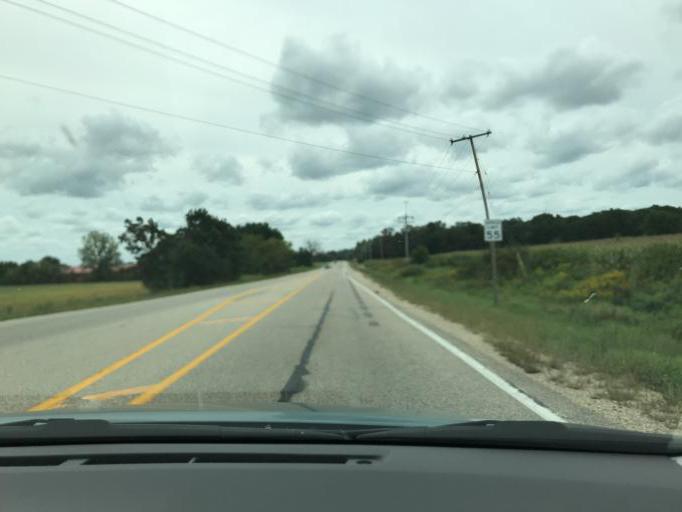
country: US
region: Wisconsin
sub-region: Racine County
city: Bohners Lake
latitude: 42.6402
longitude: -88.2502
